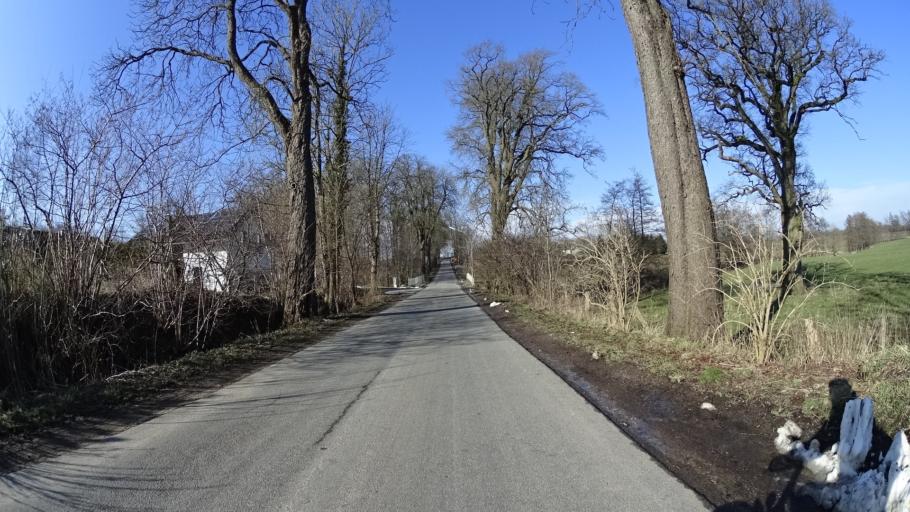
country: DE
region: Schleswig-Holstein
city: Schellhorn
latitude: 54.2510
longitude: 10.3236
